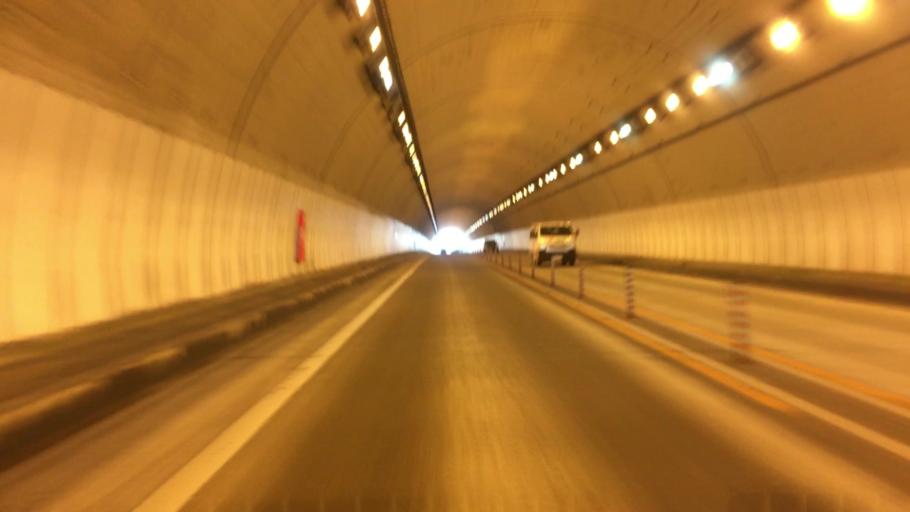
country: JP
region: Kyoto
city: Fukuchiyama
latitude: 35.2286
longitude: 135.0264
